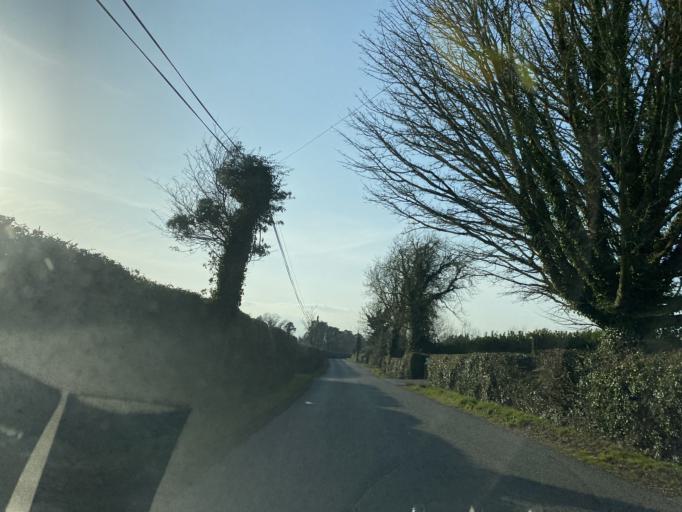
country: IE
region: Leinster
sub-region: Kildare
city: Maynooth
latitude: 53.3641
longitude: -6.5754
